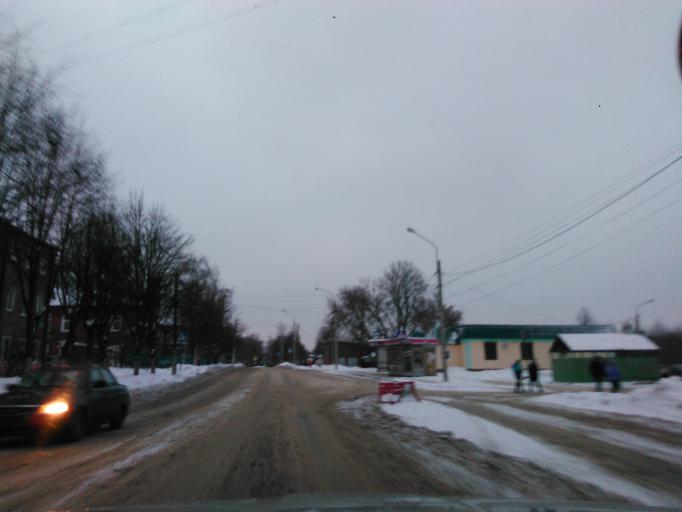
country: RU
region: Moskovskaya
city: Yakhroma
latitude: 56.2872
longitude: 37.4868
